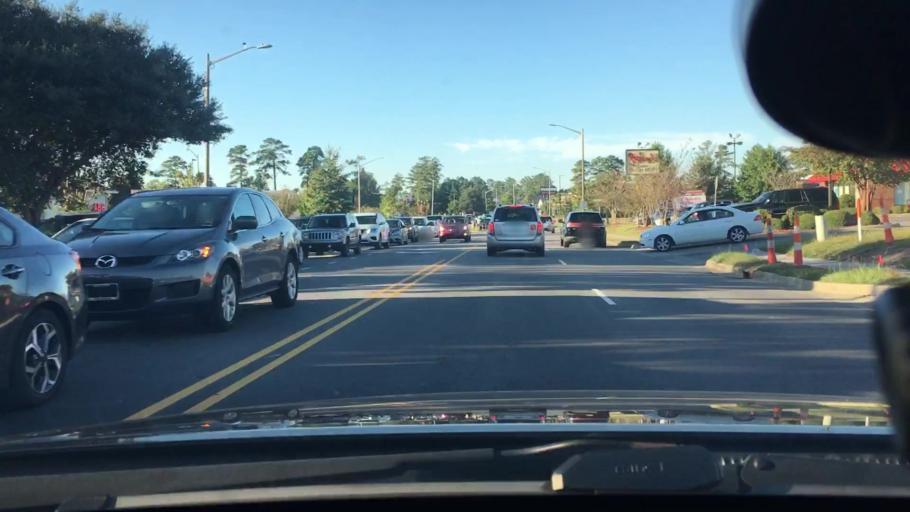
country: US
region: North Carolina
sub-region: Pitt County
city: Windsor
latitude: 35.5663
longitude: -77.3561
